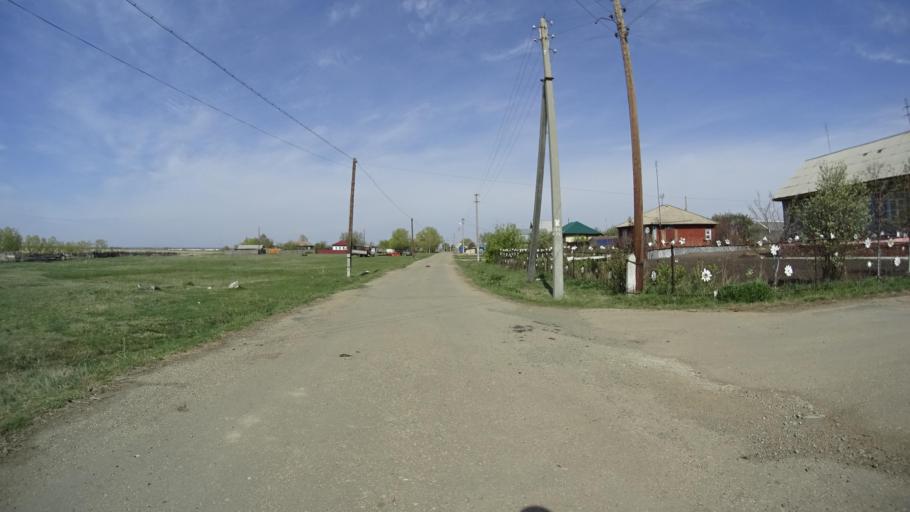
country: RU
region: Chelyabinsk
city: Chesma
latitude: 53.7981
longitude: 61.0220
